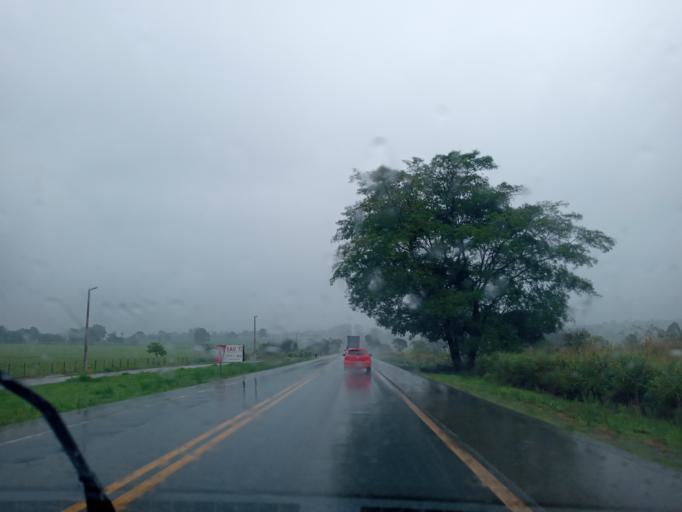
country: BR
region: Minas Gerais
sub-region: Luz
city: Luz
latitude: -19.7811
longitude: -45.7309
